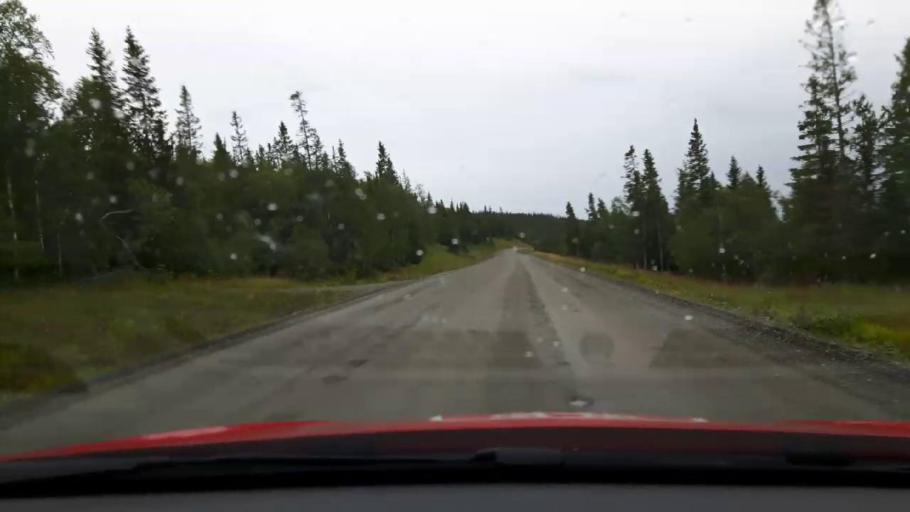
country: NO
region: Nord-Trondelag
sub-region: Meraker
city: Meraker
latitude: 63.5510
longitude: 12.3724
